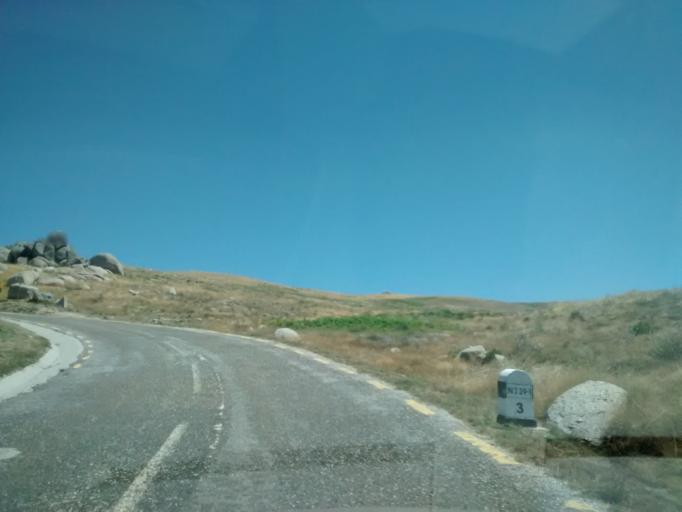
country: PT
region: Guarda
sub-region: Seia
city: Seia
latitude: 40.4155
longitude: -7.6375
